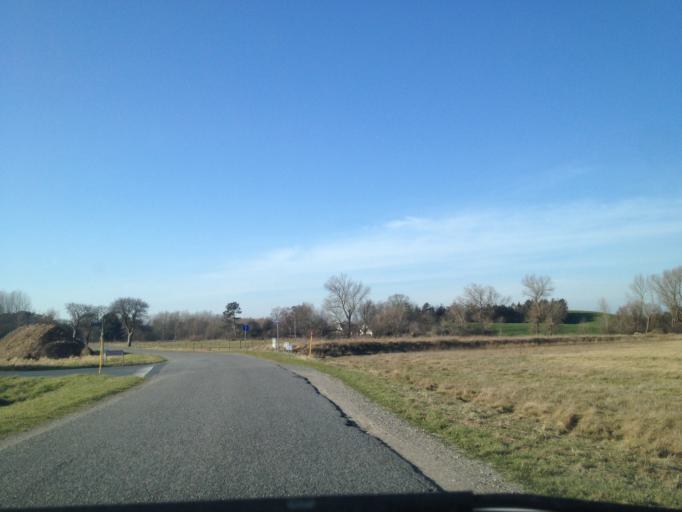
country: DK
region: South Denmark
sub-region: Kerteminde Kommune
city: Kerteminde
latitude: 55.5502
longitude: 10.6288
